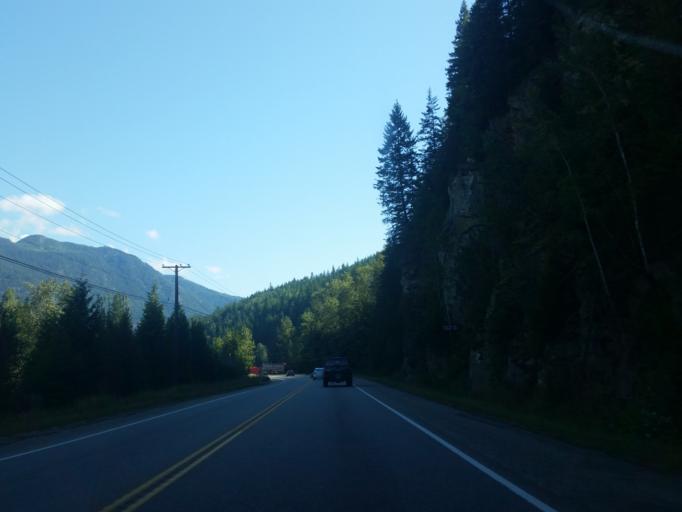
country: CA
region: British Columbia
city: Sicamous
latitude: 50.8629
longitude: -118.9313
